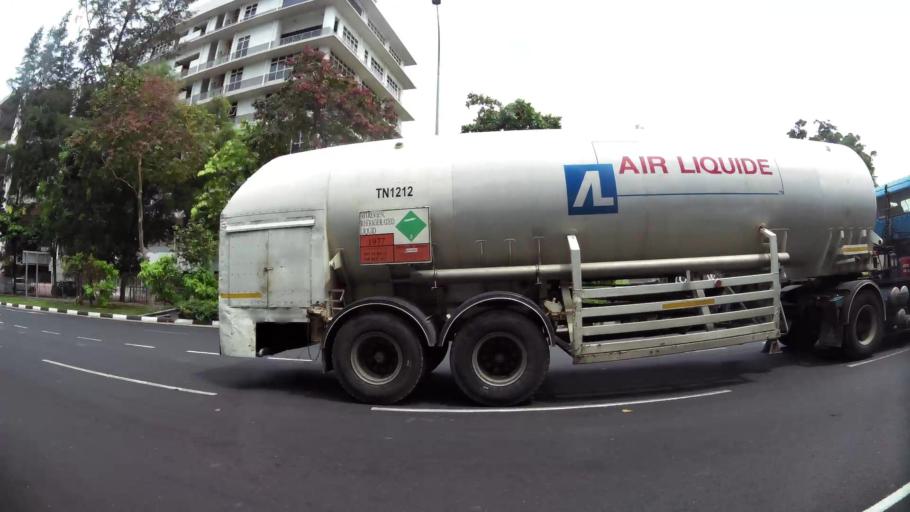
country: SG
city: Singapore
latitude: 1.3147
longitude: 103.7098
